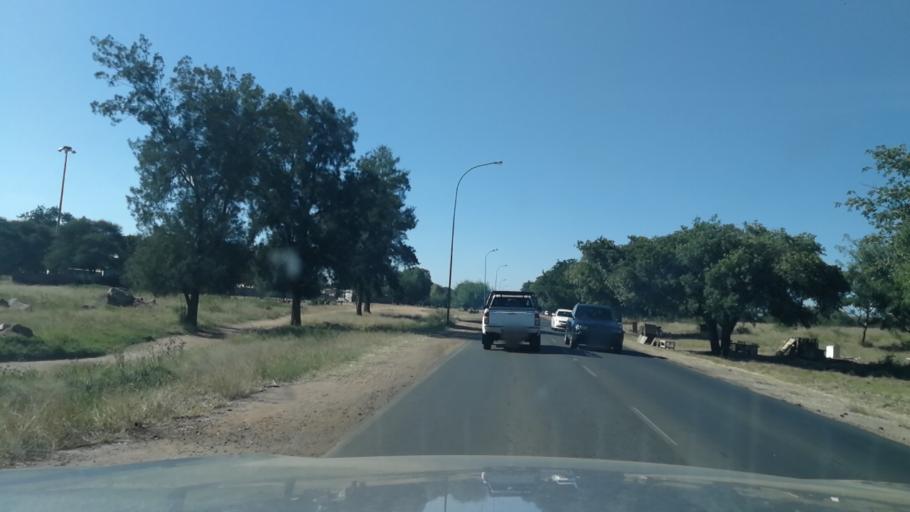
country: BW
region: South East
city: Gaborone
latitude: -24.6909
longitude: 25.8999
